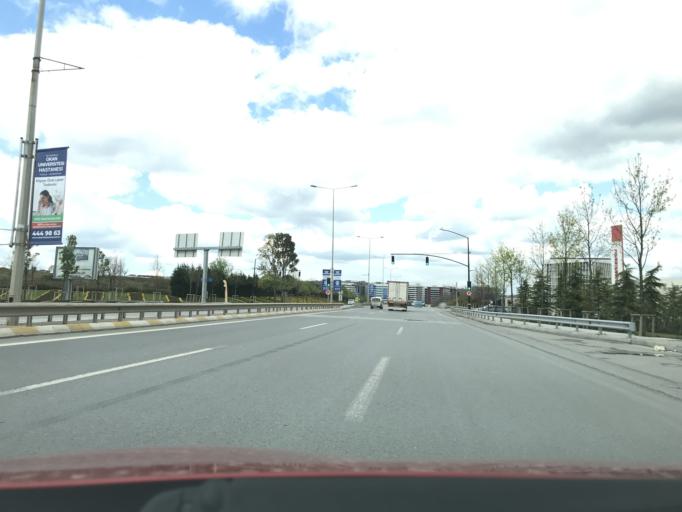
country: TR
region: Istanbul
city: Pendik
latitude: 40.9186
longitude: 29.3120
